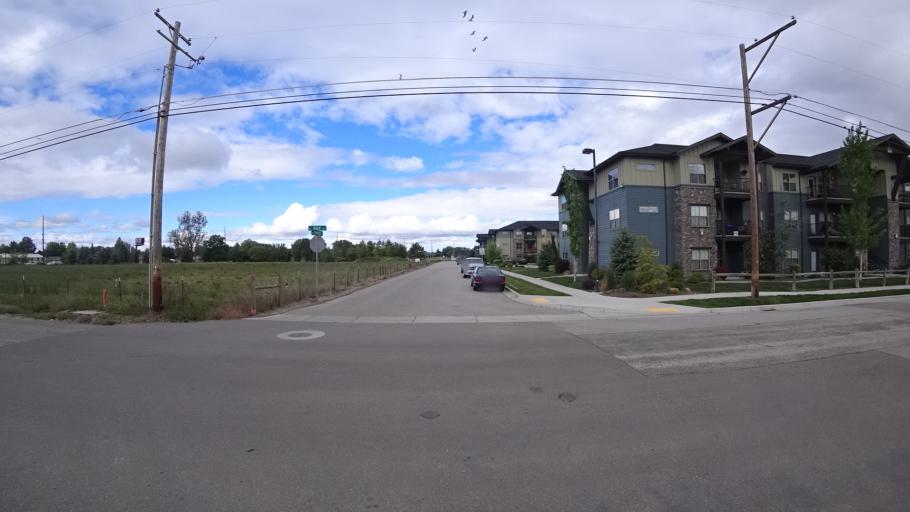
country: US
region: Idaho
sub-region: Ada County
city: Eagle
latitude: 43.6756
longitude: -116.2890
